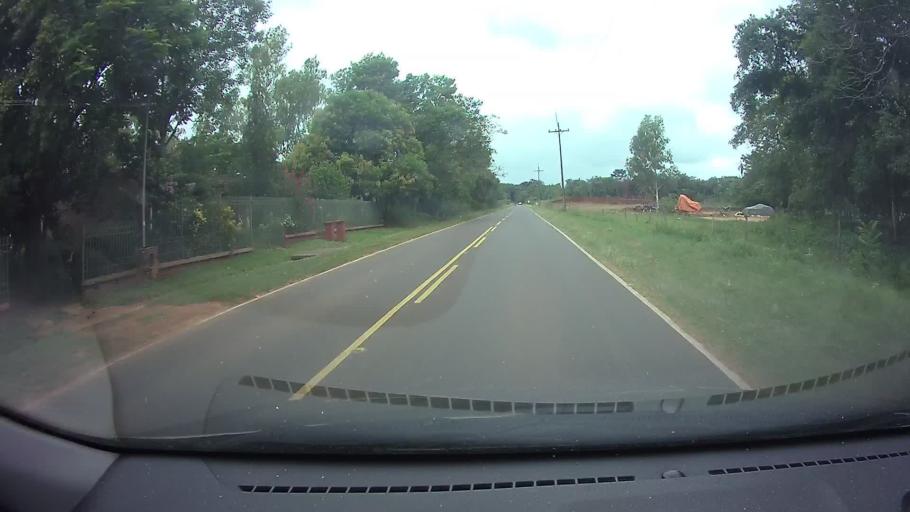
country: PY
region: Central
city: Nueva Italia
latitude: -25.6117
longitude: -57.4386
